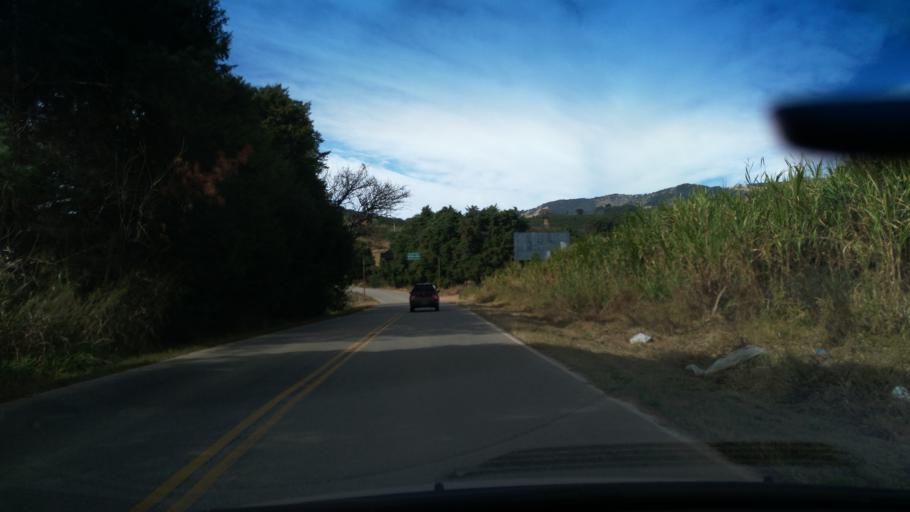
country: BR
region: Minas Gerais
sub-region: Andradas
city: Andradas
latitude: -22.0675
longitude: -46.4466
